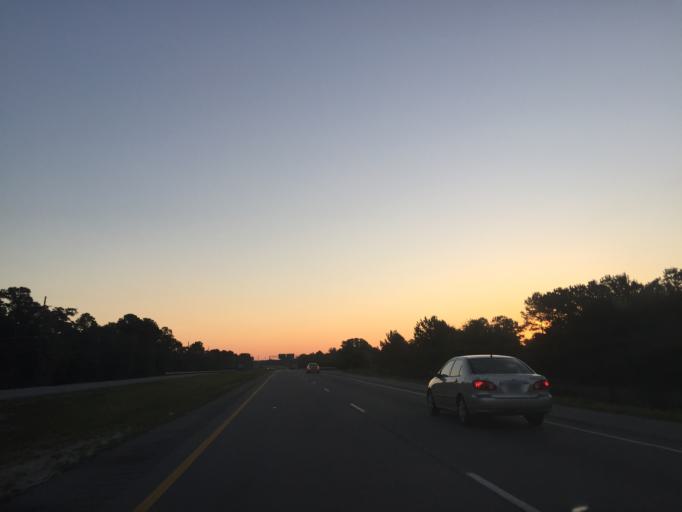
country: US
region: Georgia
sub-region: Chatham County
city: Isle of Hope
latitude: 31.9793
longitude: -81.0928
